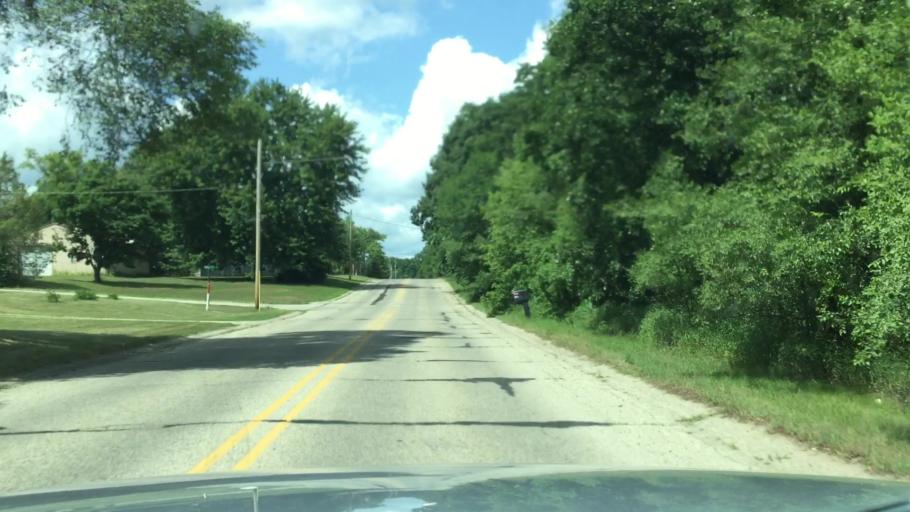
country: US
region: Michigan
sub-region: Ionia County
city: Belding
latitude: 43.1094
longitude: -85.2224
